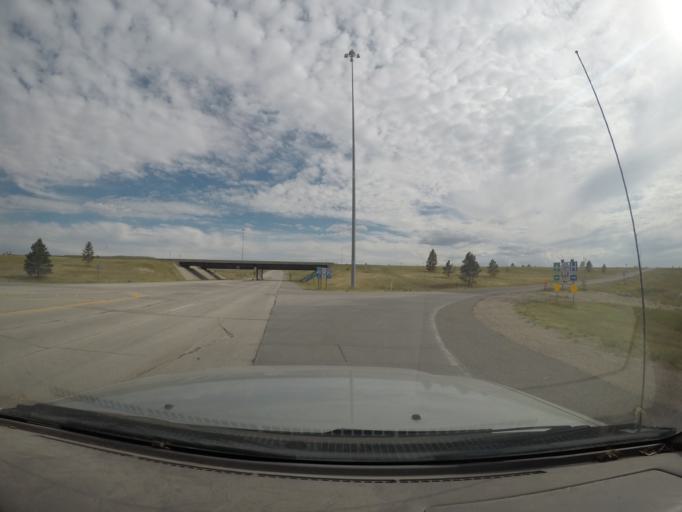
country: US
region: Nebraska
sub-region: Kimball County
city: Kimball
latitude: 41.2177
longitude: -103.6637
